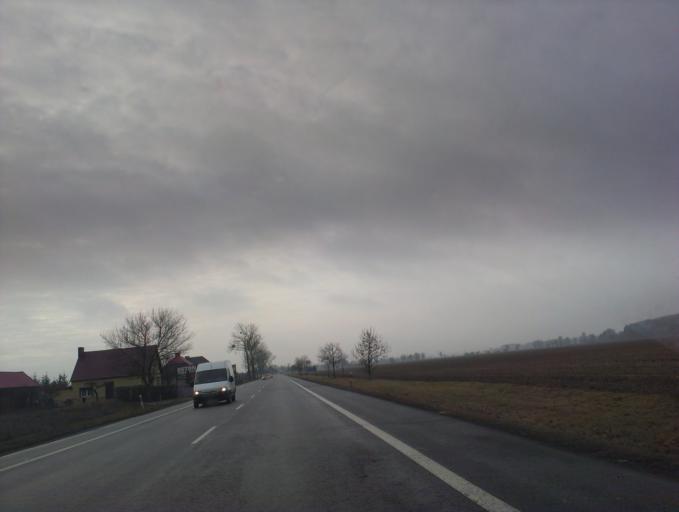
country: PL
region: Greater Poland Voivodeship
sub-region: Powiat pilski
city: Pila
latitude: 53.1067
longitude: 16.7487
